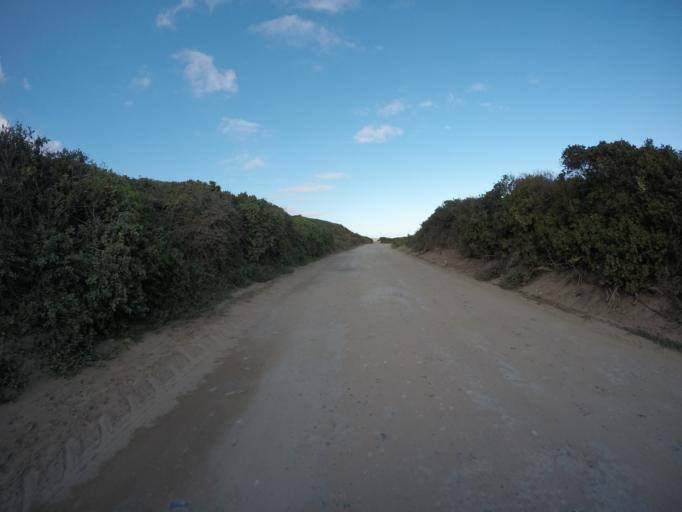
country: ZA
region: Western Cape
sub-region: Eden District Municipality
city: Riversdale
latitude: -34.4187
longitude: 21.3542
